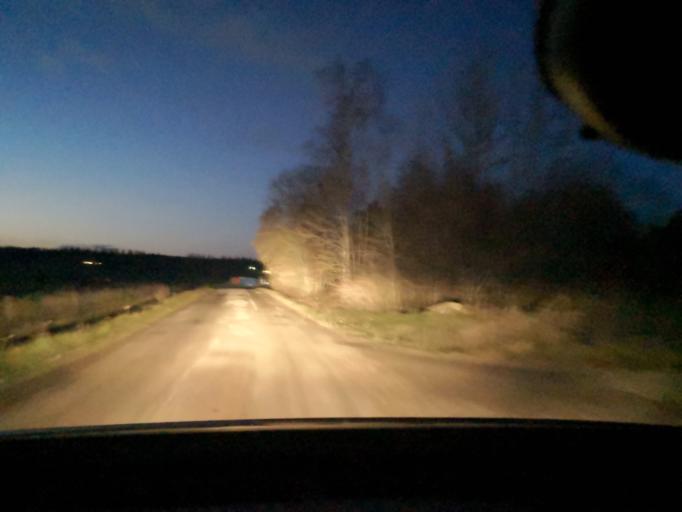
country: SE
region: Uppsala
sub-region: Heby Kommun
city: Heby
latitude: 59.9338
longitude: 16.7528
